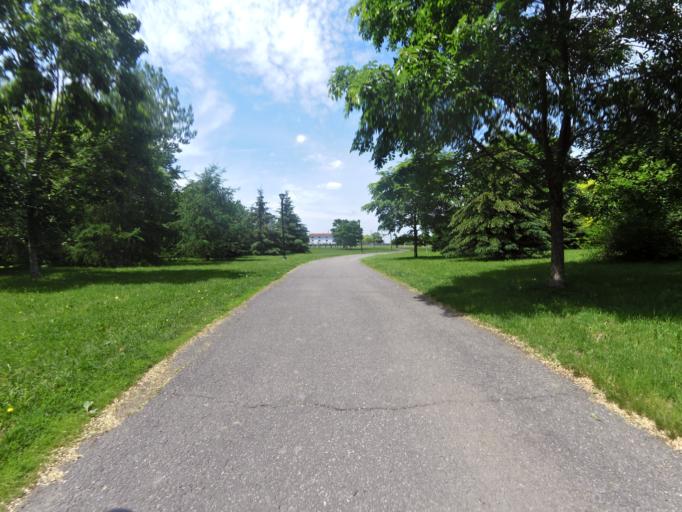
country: CA
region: Ontario
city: Ottawa
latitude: 45.3611
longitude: -75.6367
